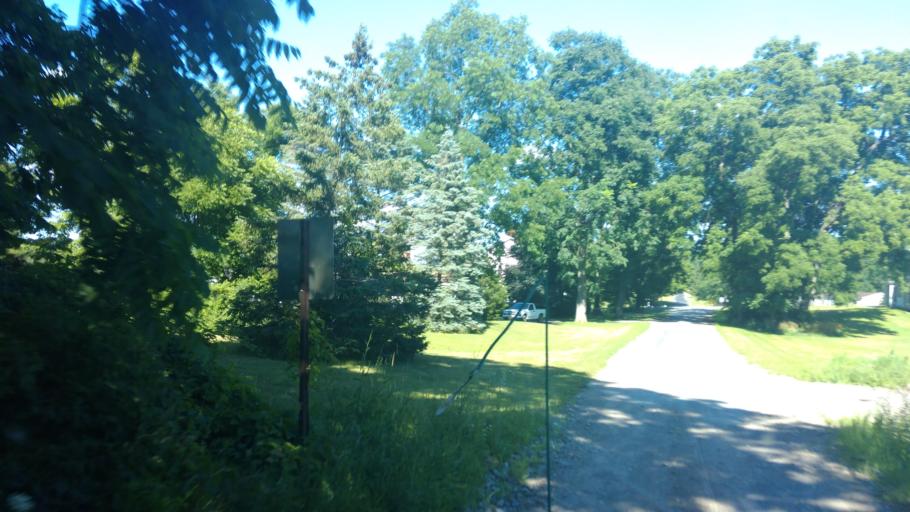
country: US
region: New York
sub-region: Wayne County
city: Clyde
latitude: 43.0272
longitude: -76.8634
